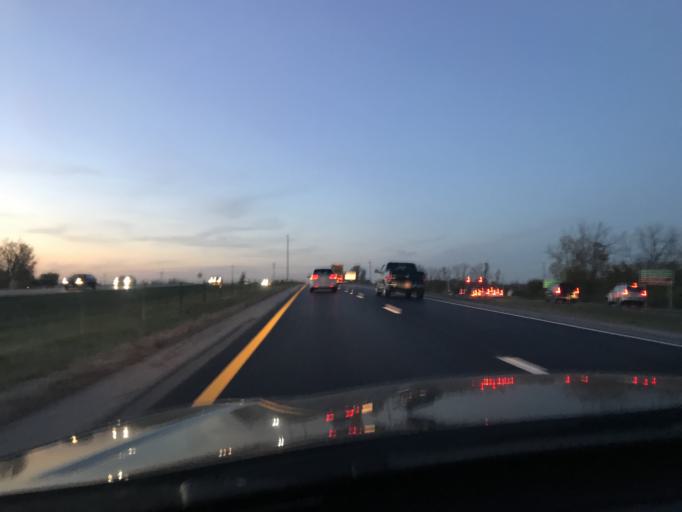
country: US
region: Ohio
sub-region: Franklin County
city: Dublin
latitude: 40.1071
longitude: -83.1784
